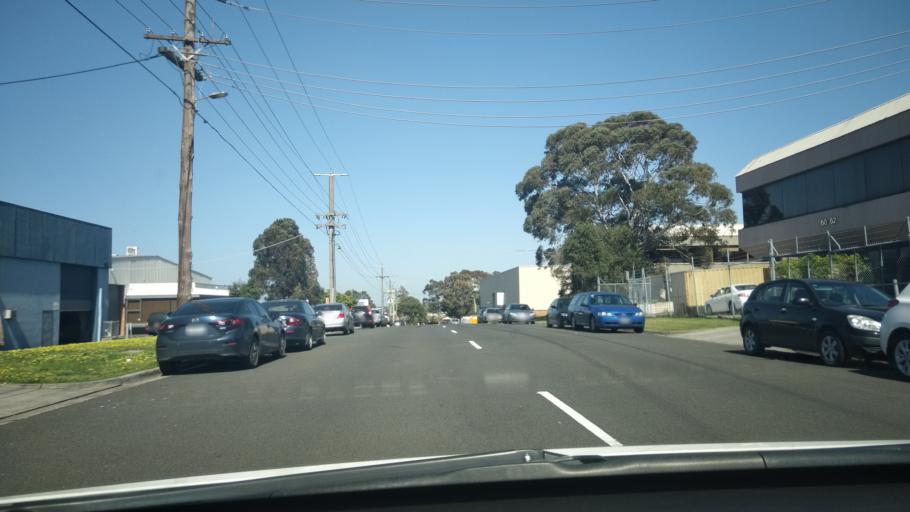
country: AU
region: Victoria
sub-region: Greater Dandenong
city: Noble Park North
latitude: -37.9558
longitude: 145.1855
